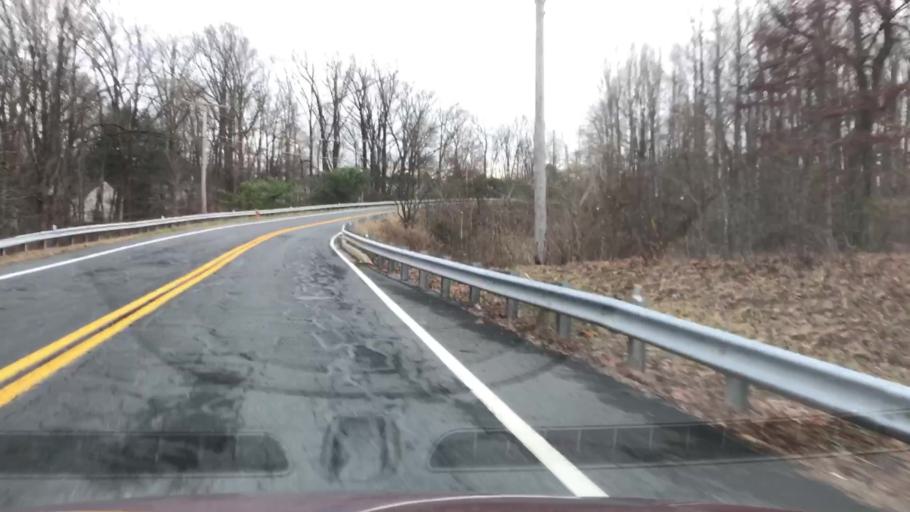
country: US
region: Maryland
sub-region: Howard County
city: Riverside
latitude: 39.1600
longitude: -76.8857
